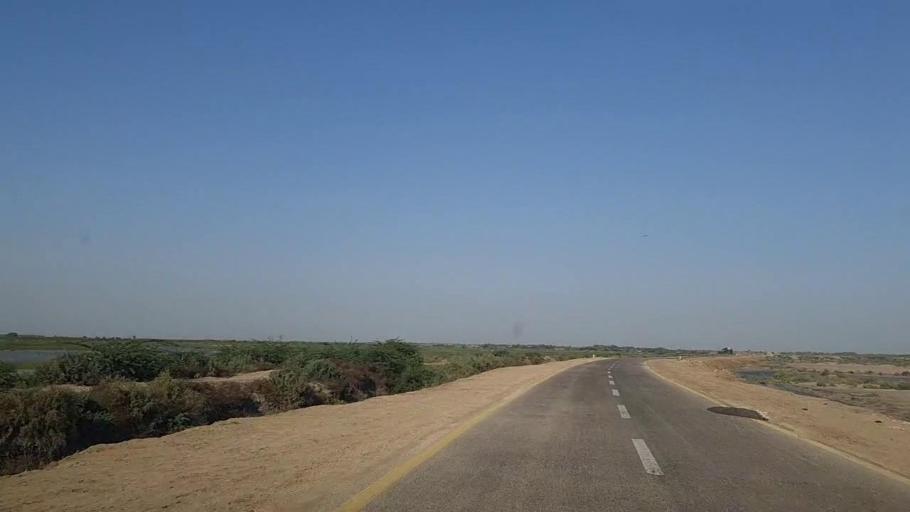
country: PK
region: Sindh
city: Jati
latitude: 24.4403
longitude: 68.3194
